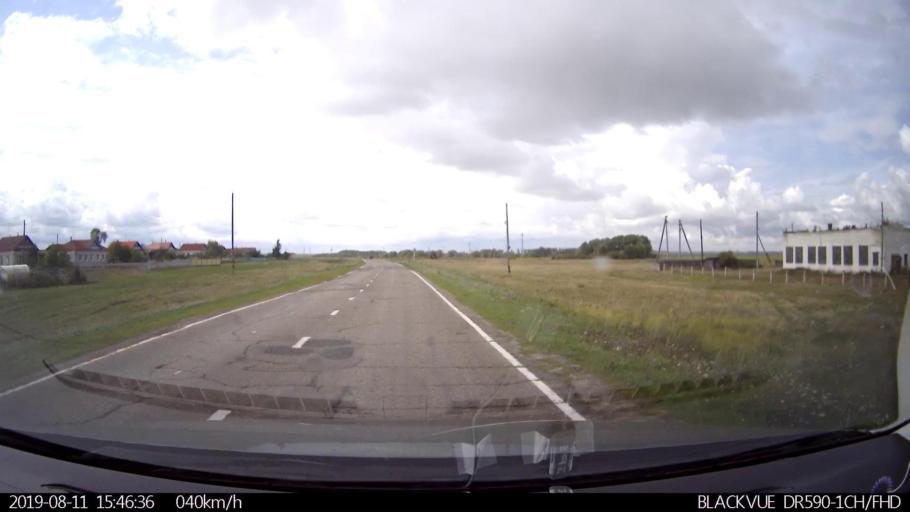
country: RU
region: Ulyanovsk
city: Ignatovka
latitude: 53.8830
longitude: 47.6555
